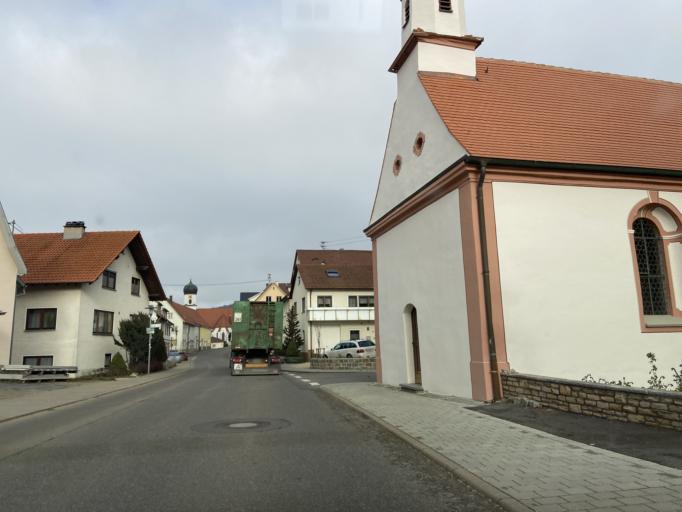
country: DE
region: Baden-Wuerttemberg
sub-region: Tuebingen Region
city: Hettingen
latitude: 48.2143
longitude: 9.2311
